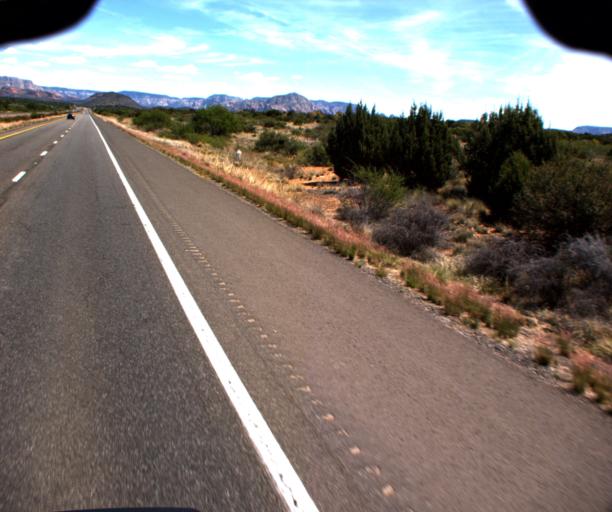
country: US
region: Arizona
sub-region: Yavapai County
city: Cornville
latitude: 34.8167
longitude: -111.9028
